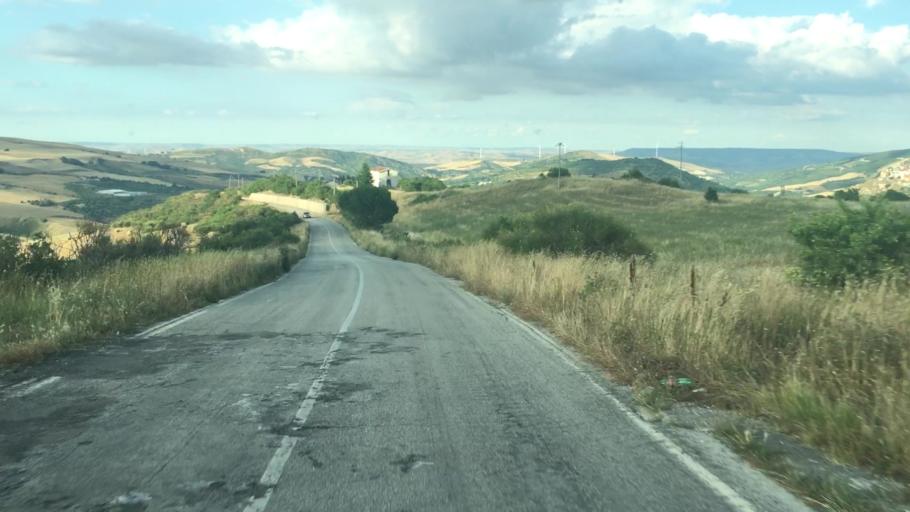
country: IT
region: Basilicate
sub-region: Provincia di Potenza
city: Tolve
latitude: 40.6943
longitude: 15.9905
